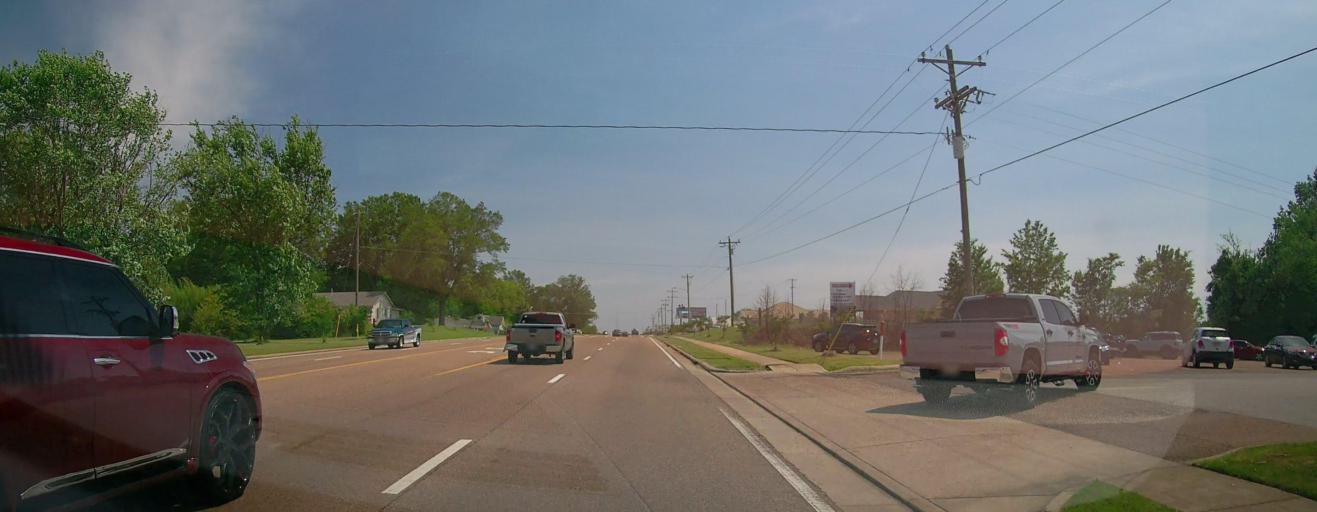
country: US
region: Mississippi
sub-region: De Soto County
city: Olive Branch
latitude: 34.9545
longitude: -89.8305
